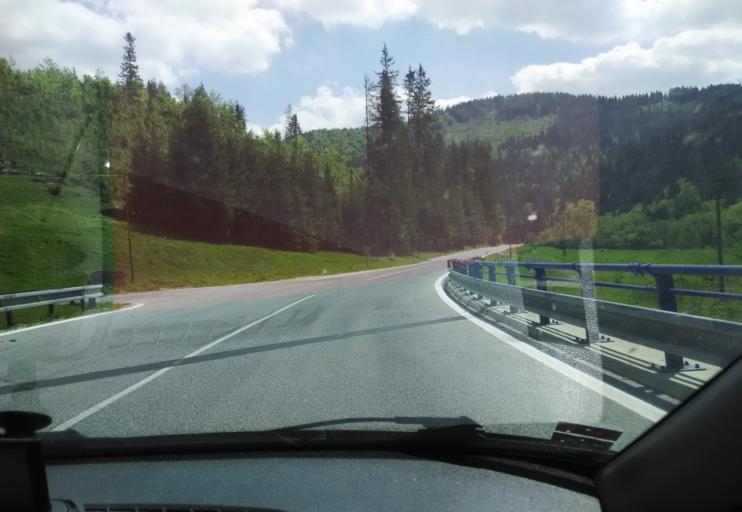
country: SK
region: Kosicky
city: Dobsina
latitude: 48.8499
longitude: 20.4275
